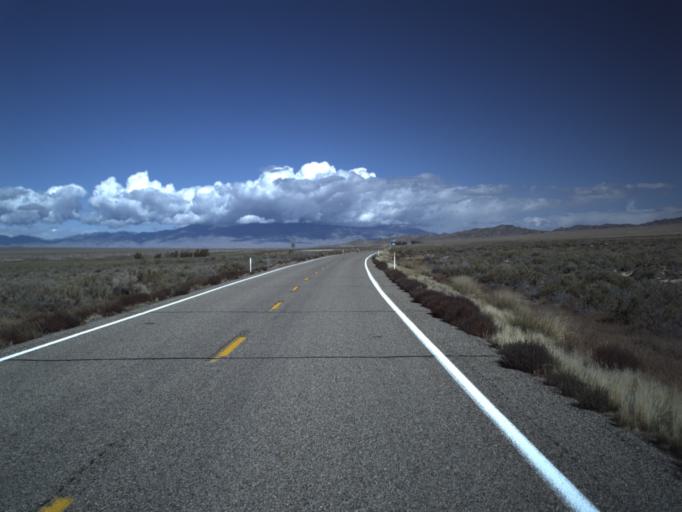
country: US
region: Nevada
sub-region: White Pine County
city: McGill
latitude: 38.8205
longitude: -113.9863
